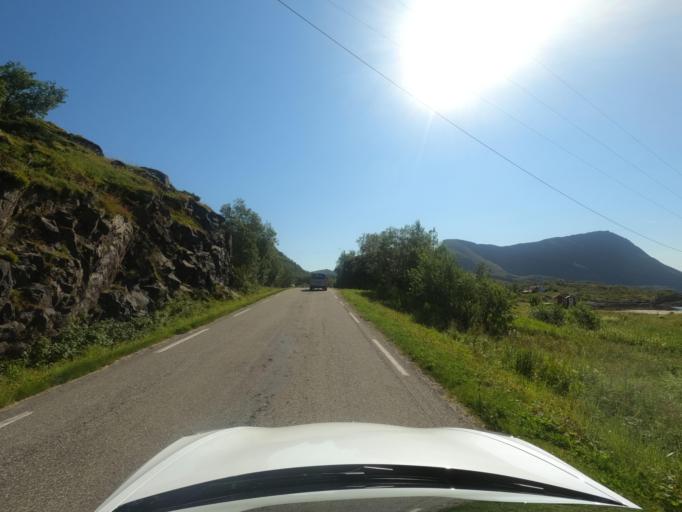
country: NO
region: Nordland
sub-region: Hadsel
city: Stokmarknes
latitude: 68.3105
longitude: 14.9890
